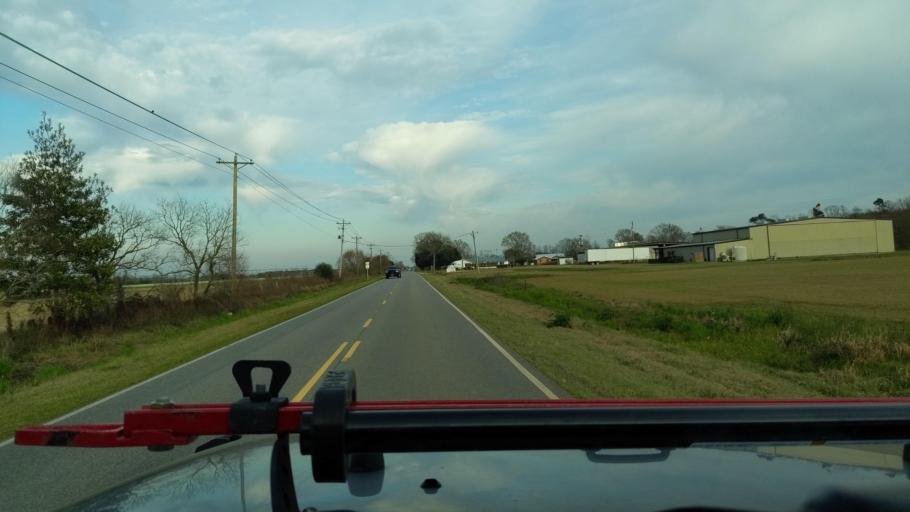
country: US
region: Alabama
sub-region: Baldwin County
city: Foley
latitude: 30.4580
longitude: -87.7158
